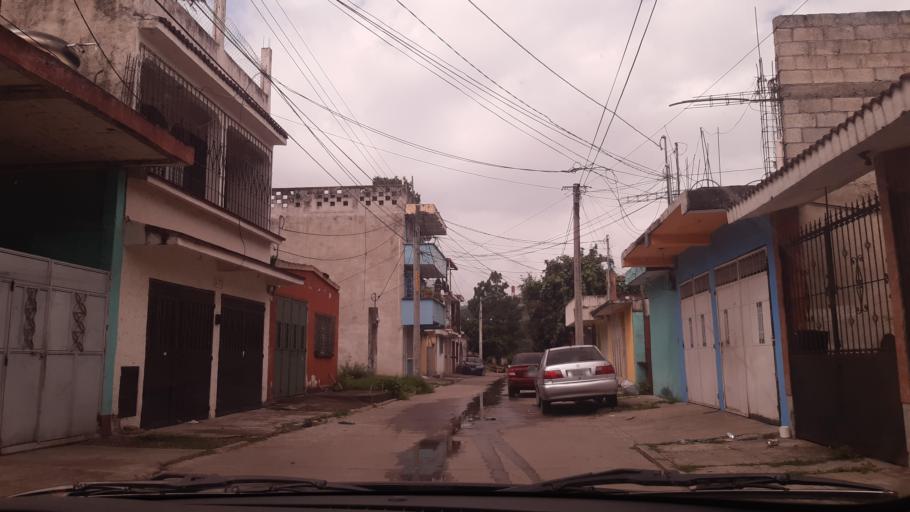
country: GT
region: Guatemala
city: Petapa
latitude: 14.5025
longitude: -90.5455
